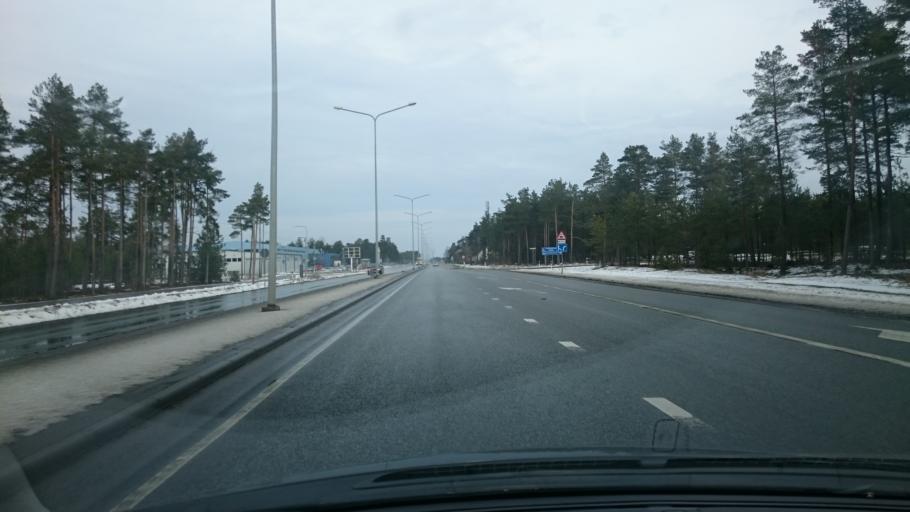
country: EE
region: Harju
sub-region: Saku vald
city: Saku
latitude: 59.3343
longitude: 24.6974
